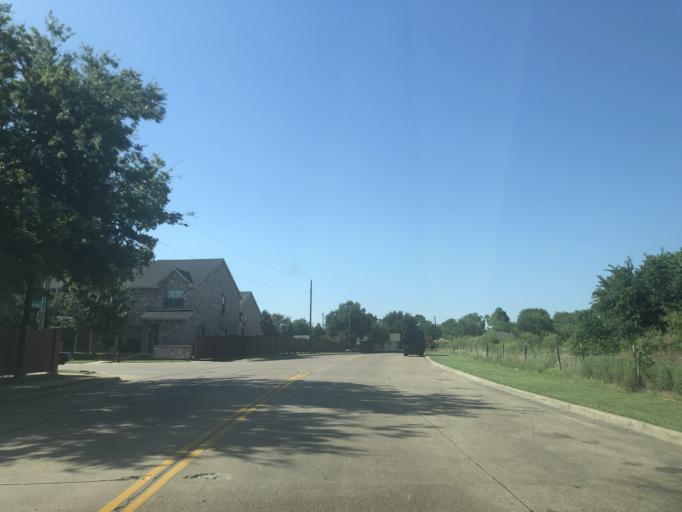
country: US
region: Texas
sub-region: Dallas County
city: Grand Prairie
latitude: 32.7521
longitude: -97.0365
